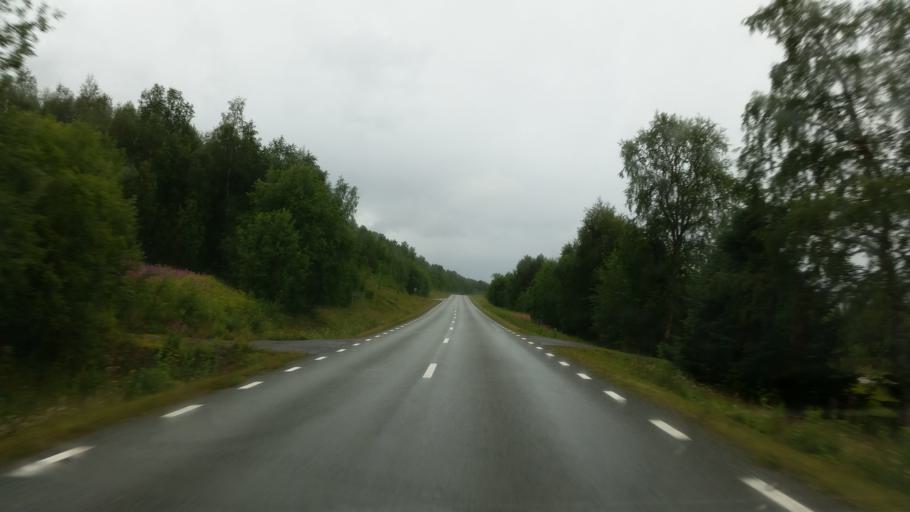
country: NO
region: Nordland
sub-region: Rana
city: Mo i Rana
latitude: 65.8606
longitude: 15.0249
